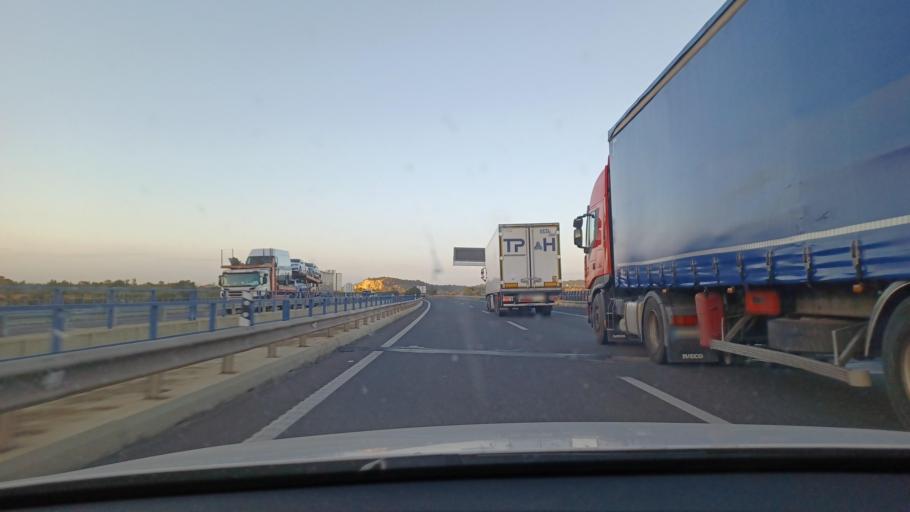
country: ES
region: Valencia
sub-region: Provincia de Castello
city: Vinaros
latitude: 40.4762
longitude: 0.4192
